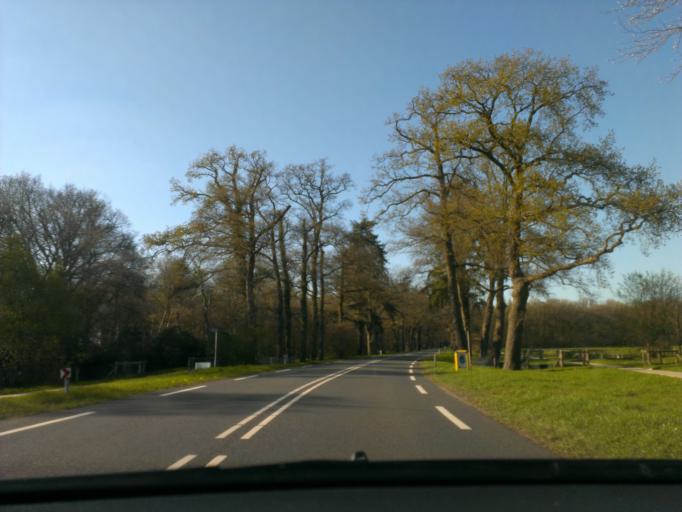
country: NL
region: Overijssel
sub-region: Gemeente Twenterand
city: Den Ham
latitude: 52.4742
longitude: 6.4640
